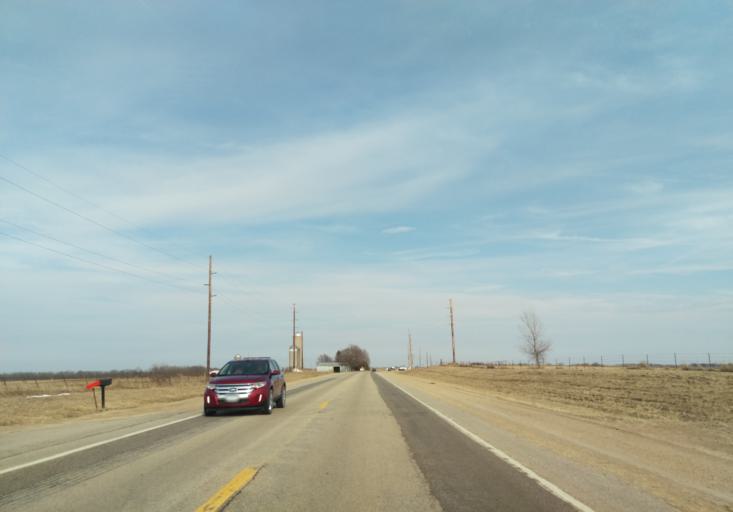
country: US
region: Wisconsin
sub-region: Grant County
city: Fennimore
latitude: 42.9750
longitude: -90.8114
